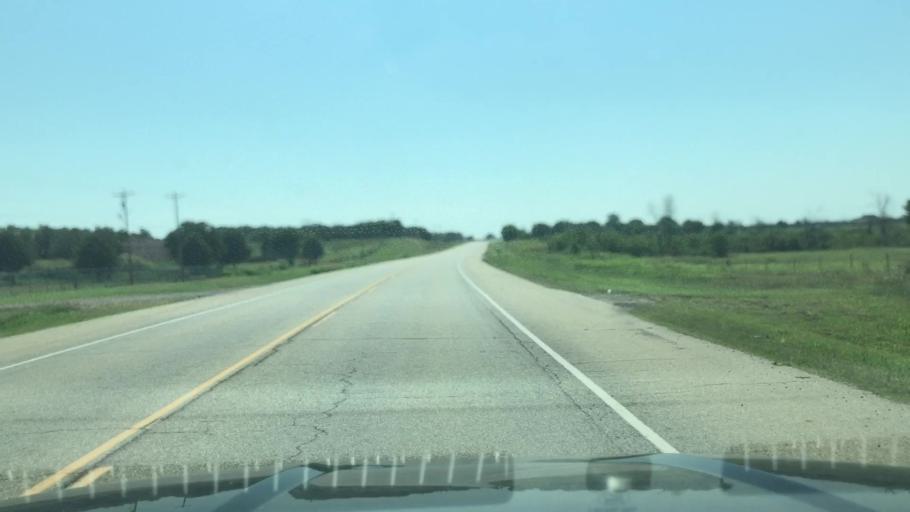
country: US
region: Oklahoma
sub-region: Creek County
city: Mannford
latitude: 36.0023
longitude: -96.3755
